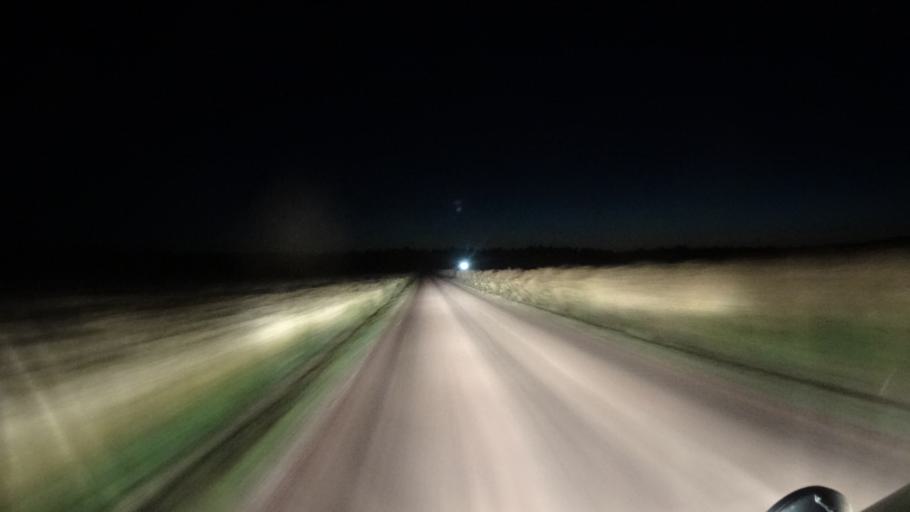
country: SE
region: OEstergoetland
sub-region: Vadstena Kommun
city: Herrestad
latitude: 58.3274
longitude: 14.8247
